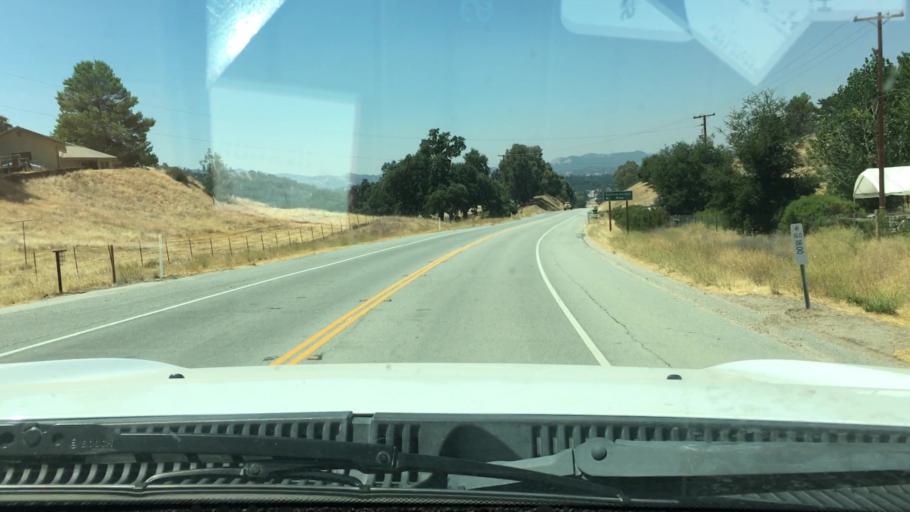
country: US
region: California
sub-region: San Luis Obispo County
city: Atascadero
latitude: 35.5070
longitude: -120.6439
